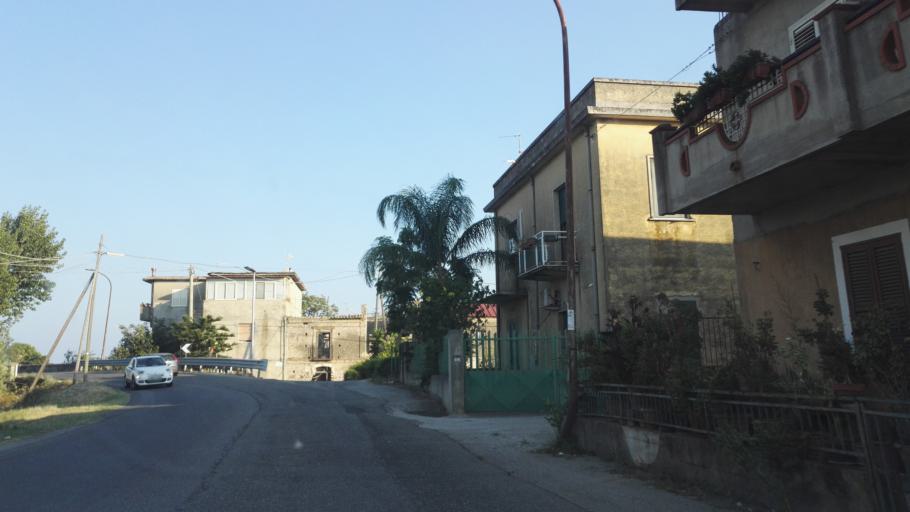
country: IT
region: Calabria
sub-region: Provincia di Reggio Calabria
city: Marina di Gioiosa Ionica
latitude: 38.3097
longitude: 16.3161
